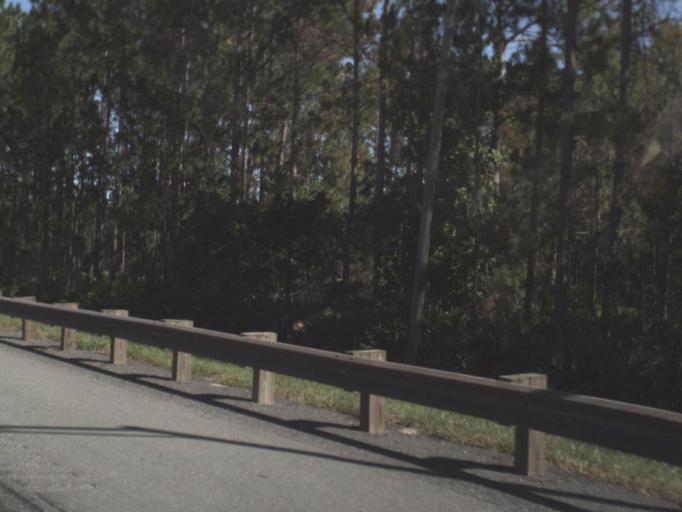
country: US
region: Florida
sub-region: Pasco County
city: Odessa
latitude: 28.2520
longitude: -82.5491
